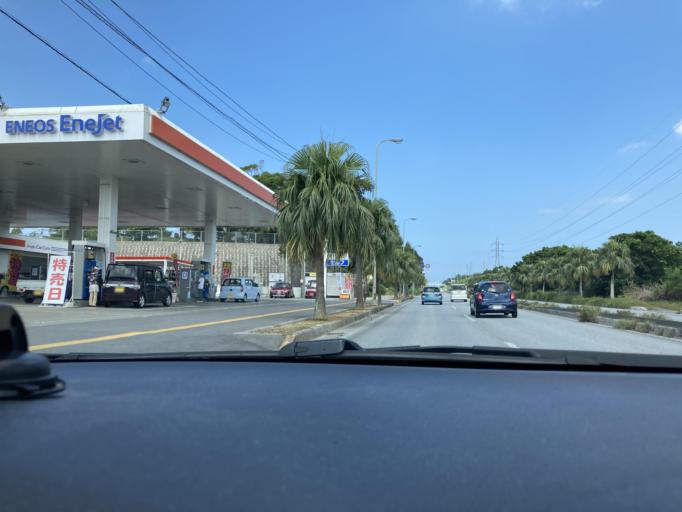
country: JP
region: Okinawa
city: Ishikawa
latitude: 26.4012
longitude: 127.7586
